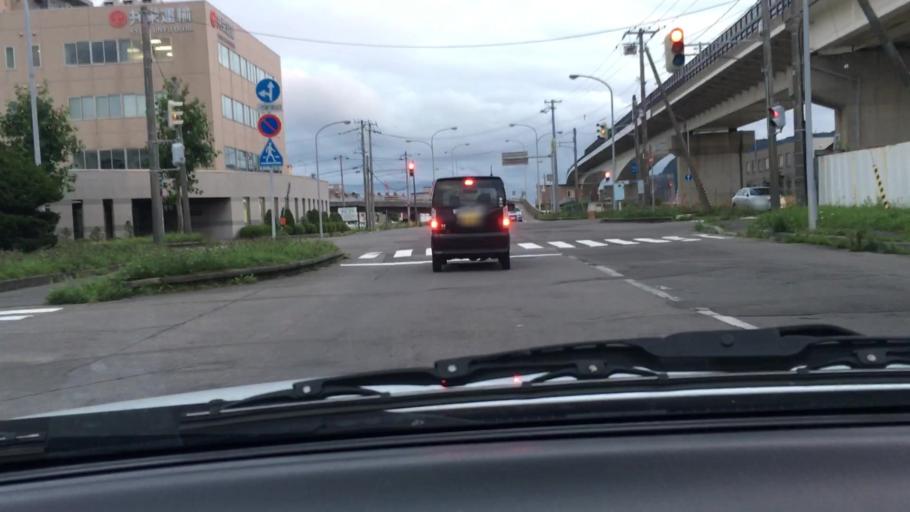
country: JP
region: Hokkaido
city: Hakodate
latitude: 41.7833
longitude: 140.7270
